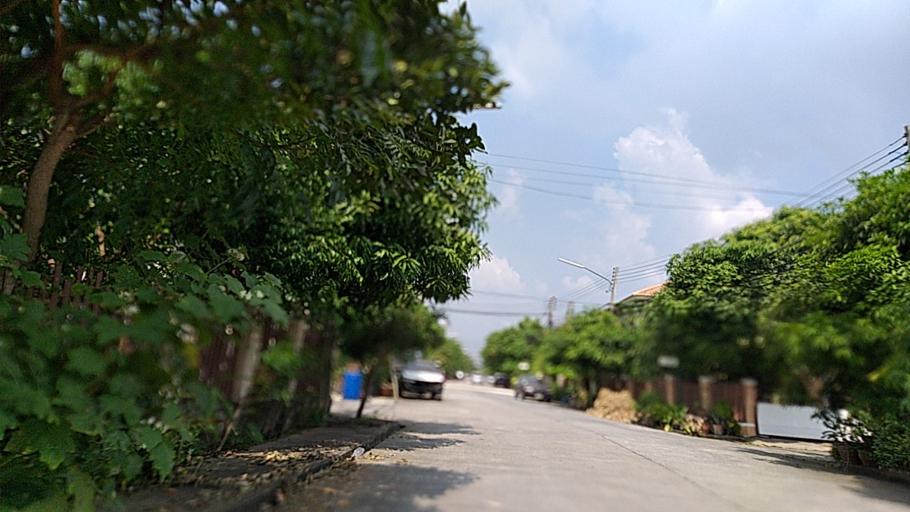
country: TH
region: Pathum Thani
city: Ban Rangsit
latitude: 14.0421
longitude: 100.7653
